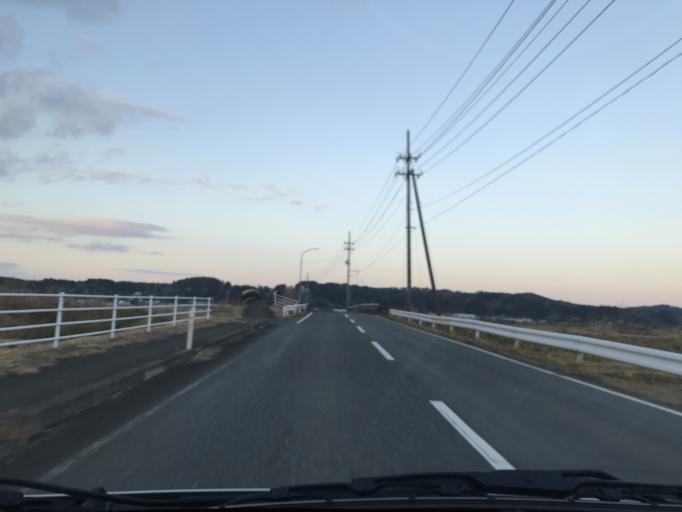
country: JP
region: Iwate
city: Ichinoseki
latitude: 38.7926
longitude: 141.1205
